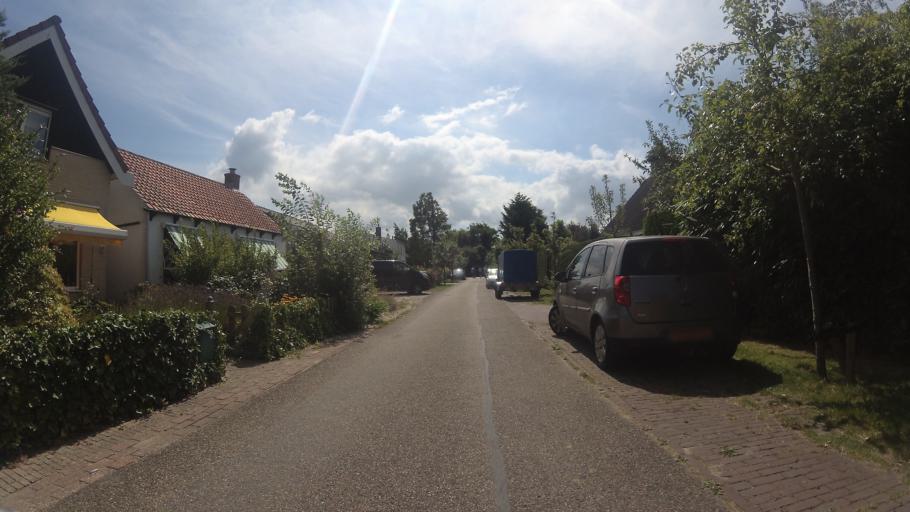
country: NL
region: Zeeland
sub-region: Schouwen-Duiveland
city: Burgh
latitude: 51.6897
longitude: 3.7317
